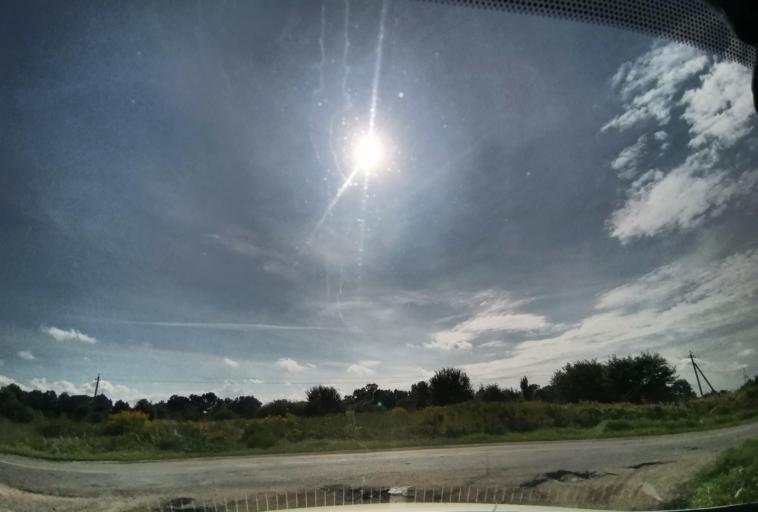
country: RU
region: Kaliningrad
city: Chernyakhovsk
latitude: 54.6517
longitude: 21.8456
